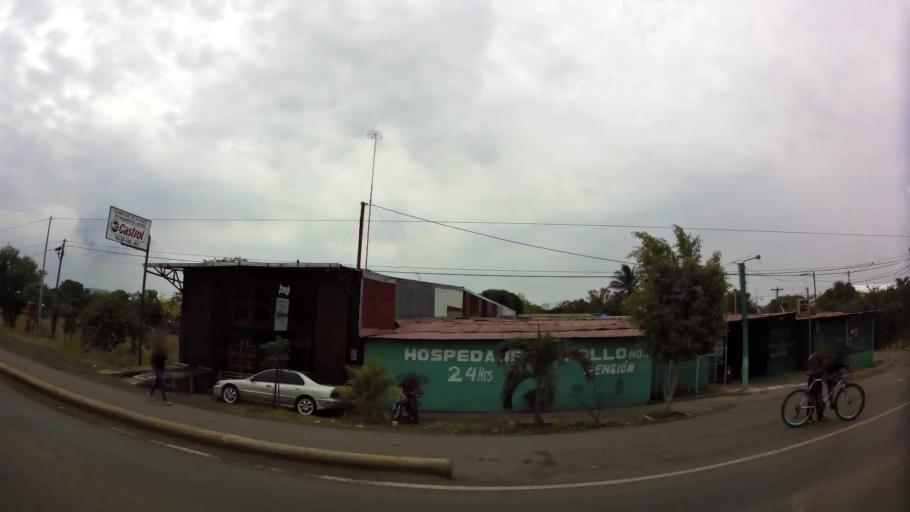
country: NI
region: Masaya
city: Masaya
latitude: 11.9726
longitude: -86.0786
